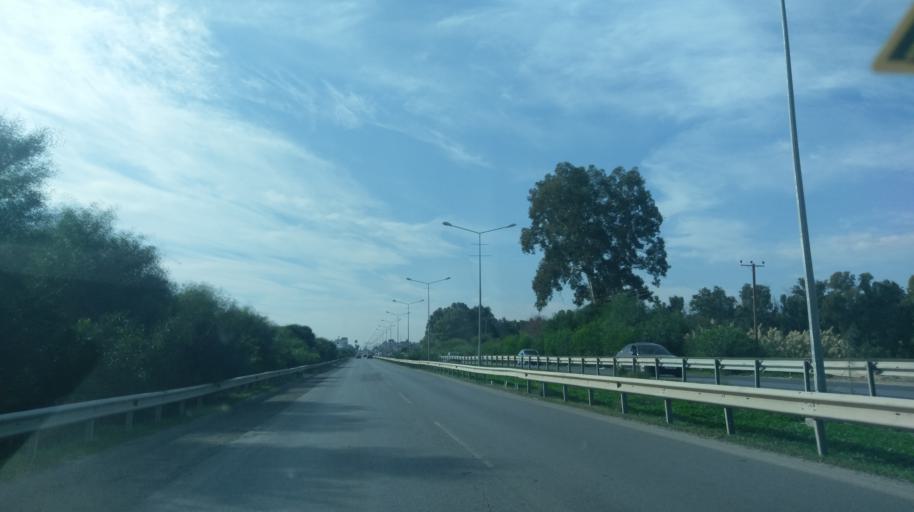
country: CY
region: Lefkosia
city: Nicosia
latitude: 35.2139
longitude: 33.3930
